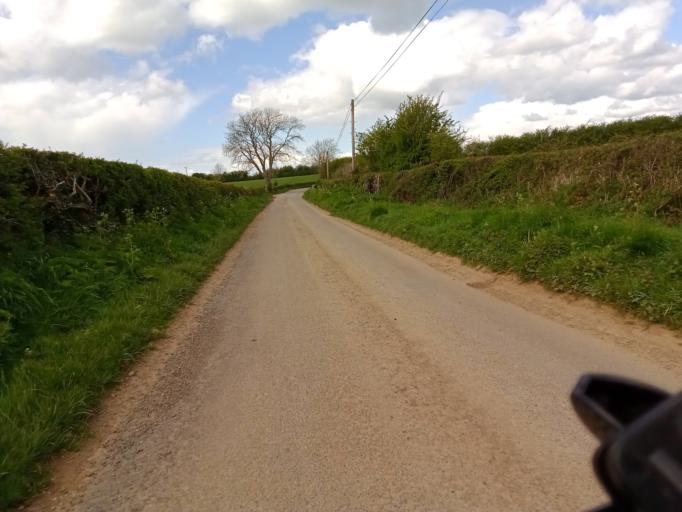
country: IE
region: Leinster
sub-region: Kilkenny
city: Thomastown
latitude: 52.5933
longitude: -7.1497
